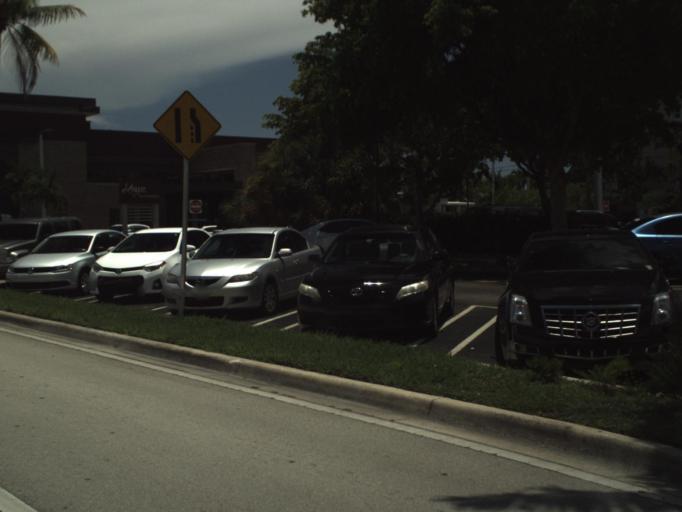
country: US
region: Florida
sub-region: Broward County
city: Lauderdale-by-the-Sea
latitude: 26.1898
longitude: -80.1043
